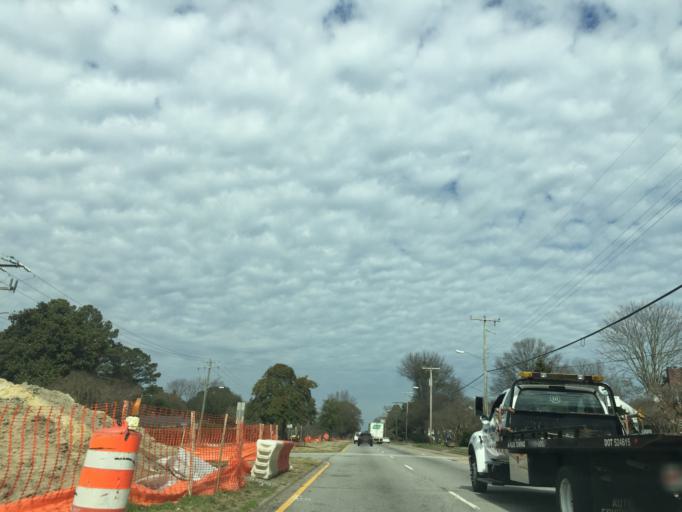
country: US
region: Virginia
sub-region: City of Norfolk
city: Norfolk
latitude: 36.9000
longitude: -76.2790
